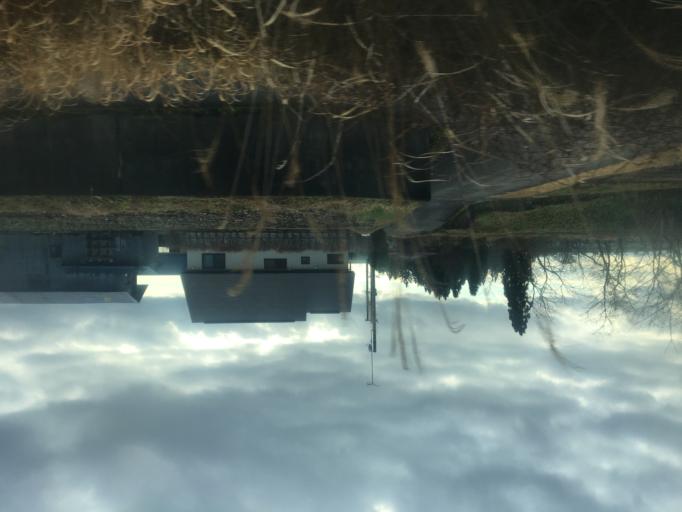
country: JP
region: Akita
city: Odate
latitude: 40.2782
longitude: 140.5066
